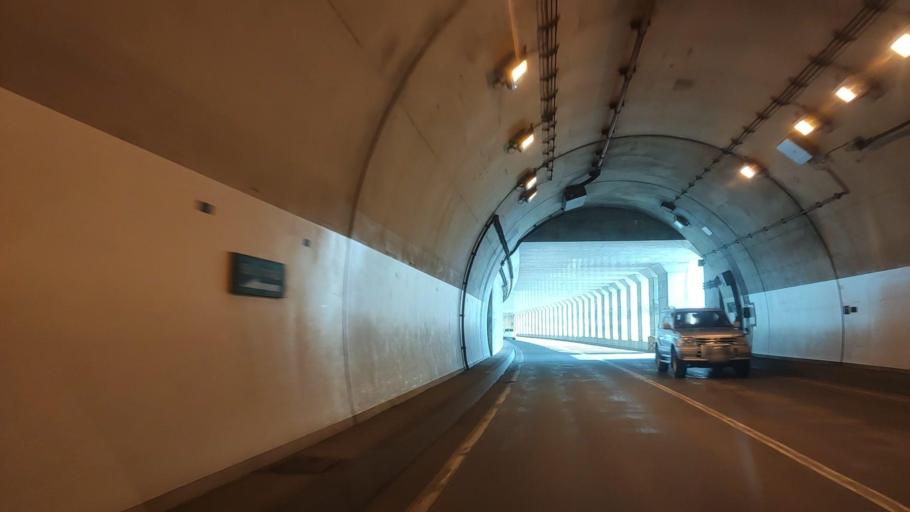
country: JP
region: Hokkaido
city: Rumoi
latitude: 43.6735
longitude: 141.3470
